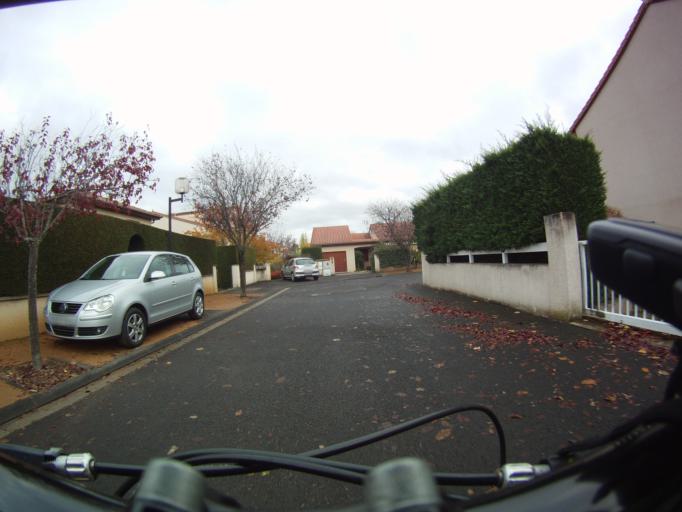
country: FR
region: Auvergne
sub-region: Departement du Puy-de-Dome
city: Aubiere
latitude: 45.7526
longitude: 3.0989
